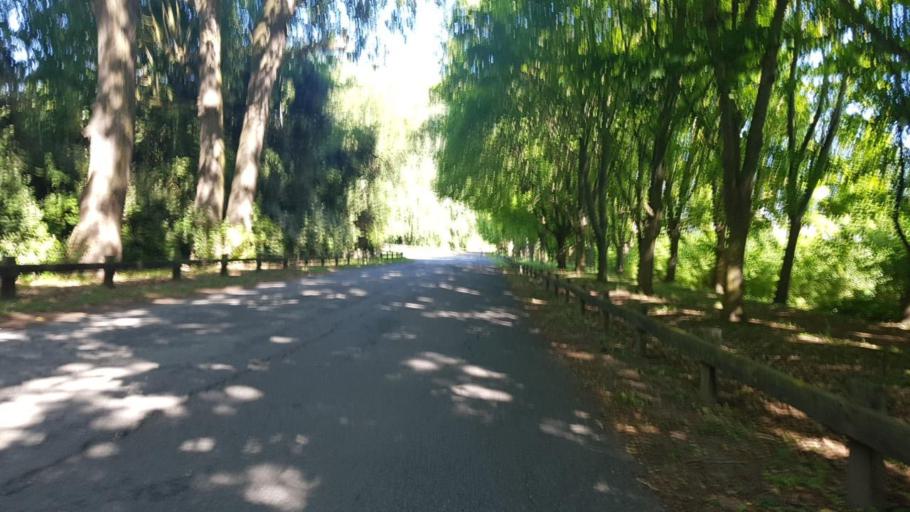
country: FR
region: Ile-de-France
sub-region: Departement de Seine-et-Marne
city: Annet-sur-Marne
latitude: 48.9165
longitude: 2.7309
